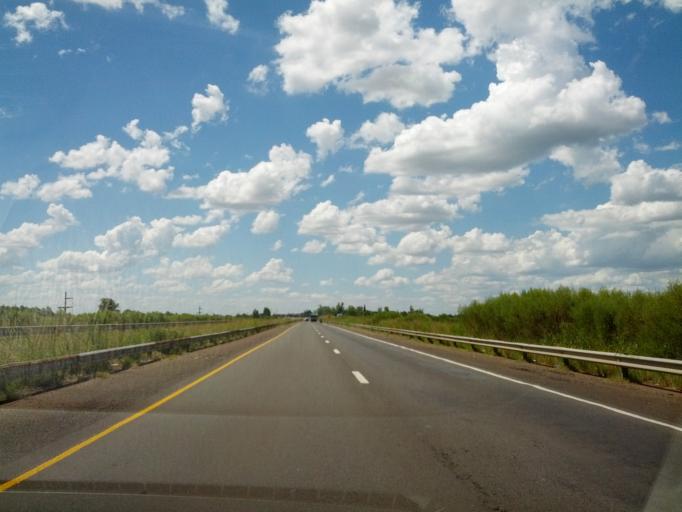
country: AR
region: Entre Rios
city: Concepcion del Uruguay
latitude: -32.4185
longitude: -58.2813
